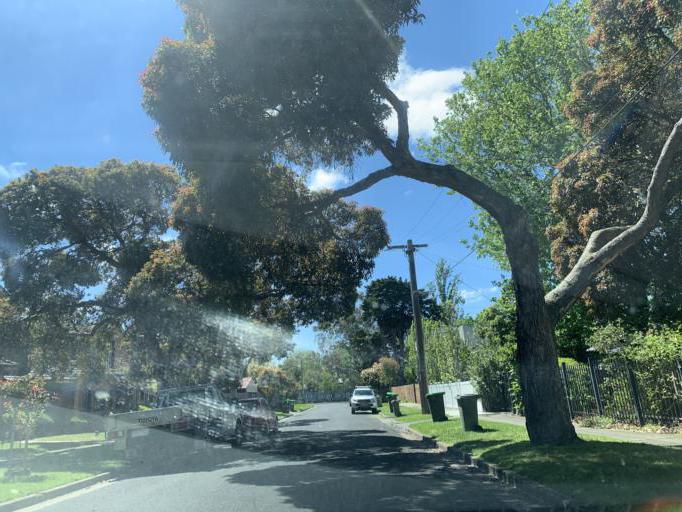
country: AU
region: Victoria
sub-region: Bayside
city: Brighton East
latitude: -37.9067
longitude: 145.0158
